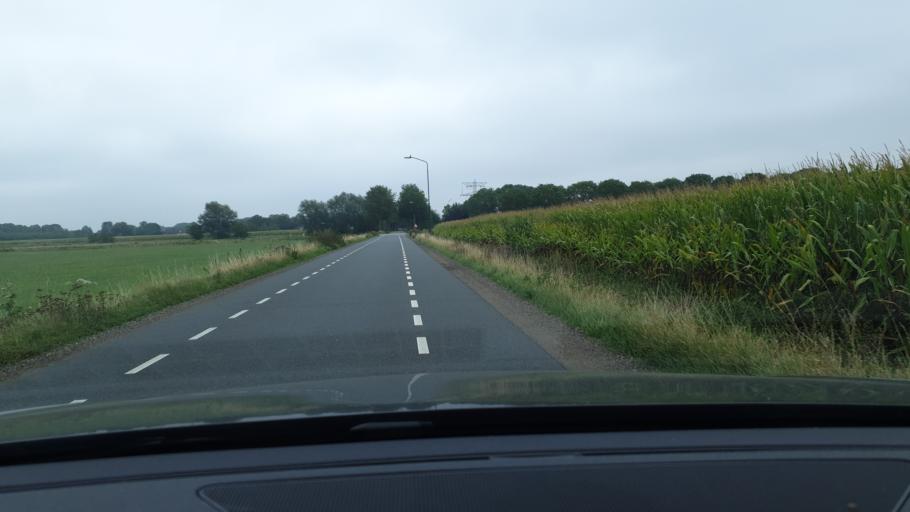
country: NL
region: North Brabant
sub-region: Gemeente Oss
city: Oss
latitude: 51.7721
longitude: 5.4859
